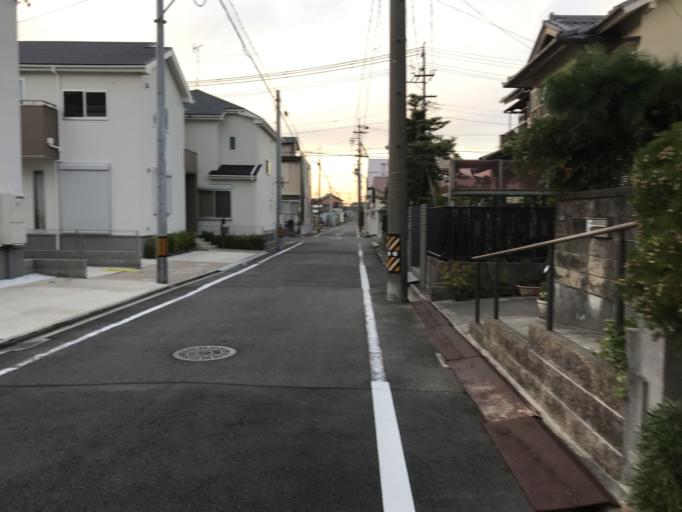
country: JP
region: Aichi
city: Nagoya-shi
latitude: 35.1928
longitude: 136.8524
